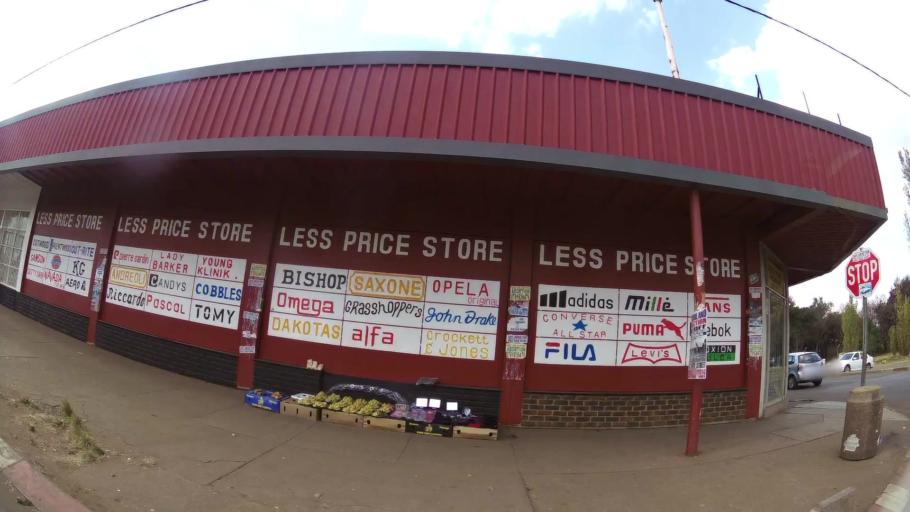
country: ZA
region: Mpumalanga
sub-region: Nkangala District Municipality
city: Delmas
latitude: -26.1520
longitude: 28.6798
